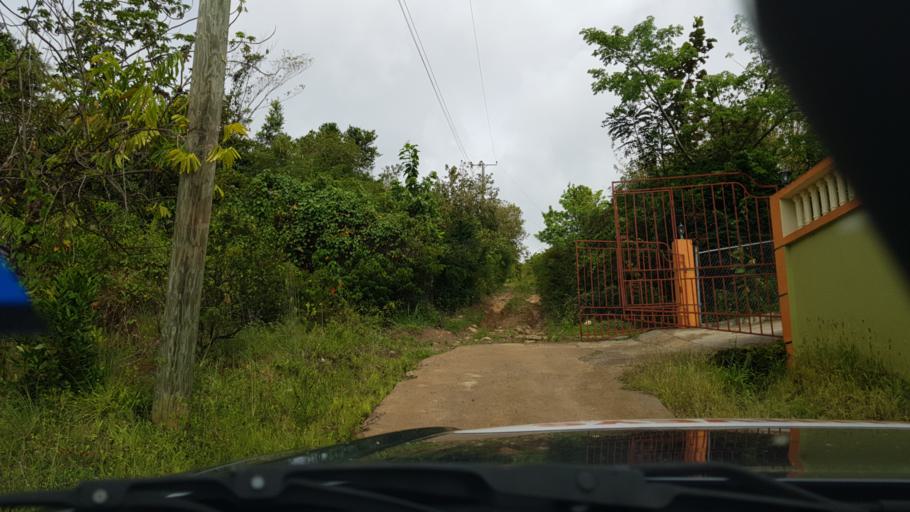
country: LC
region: Anse-la-Raye
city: Anse La Raye
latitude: 13.9440
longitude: -61.0293
